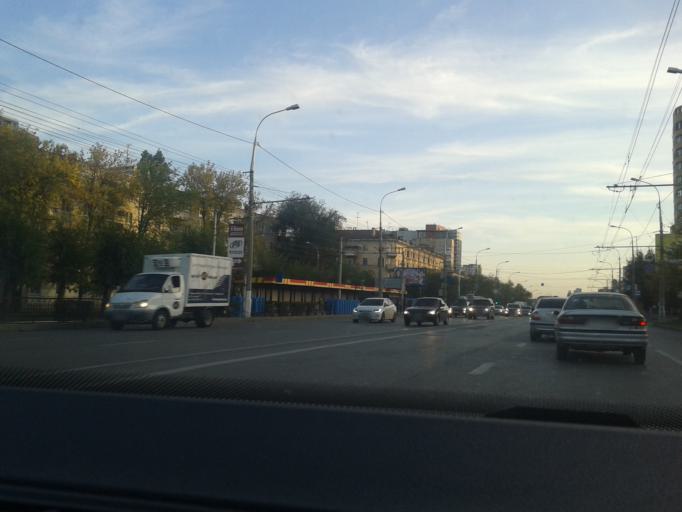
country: RU
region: Volgograd
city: Volgograd
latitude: 48.7308
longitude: 44.5402
